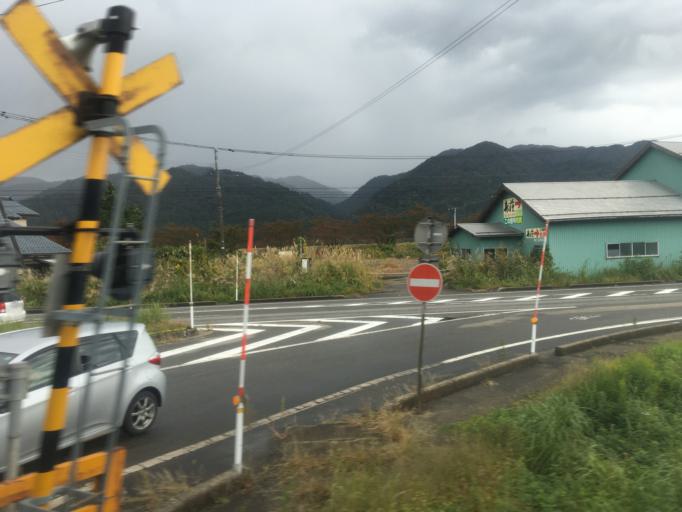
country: JP
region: Niigata
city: Murakami
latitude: 38.0792
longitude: 139.5784
